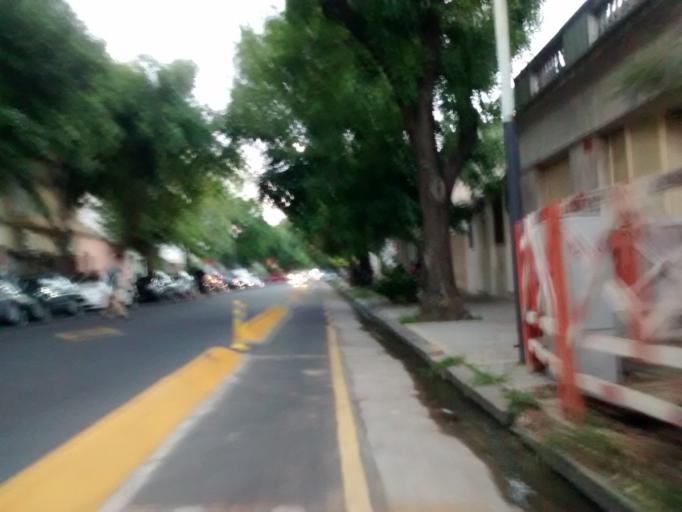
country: AR
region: Buenos Aires F.D.
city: Villa Santa Rita
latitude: -34.6078
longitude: -58.4578
